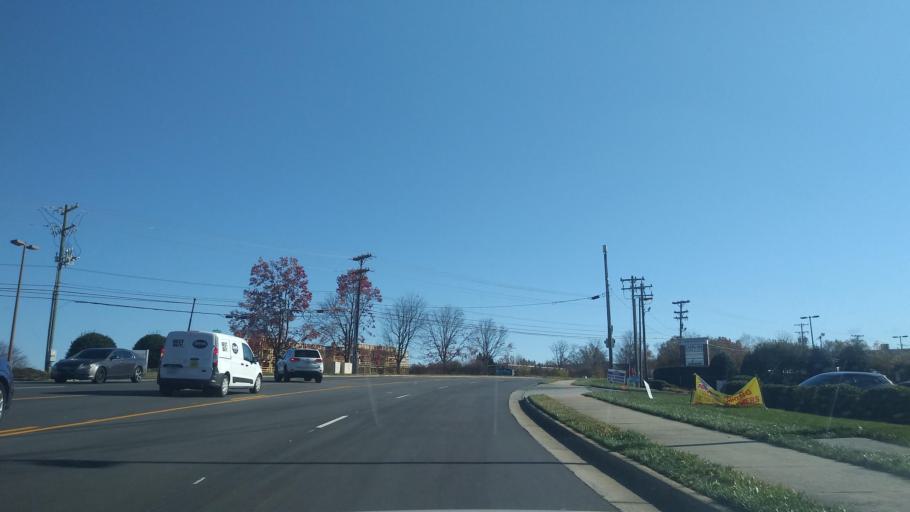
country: US
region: North Carolina
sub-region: Guilford County
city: Jamestown
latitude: 36.0537
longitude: -79.8909
